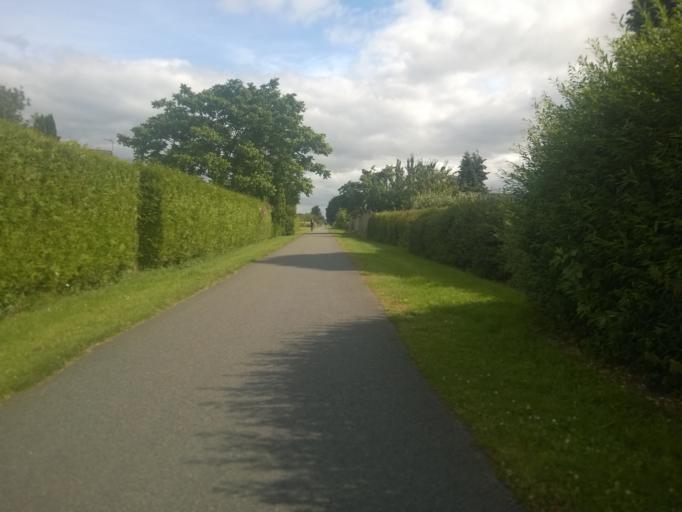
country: SE
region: Skane
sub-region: Kristianstads Kommun
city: Kristianstad
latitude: 56.0534
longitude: 14.1724
